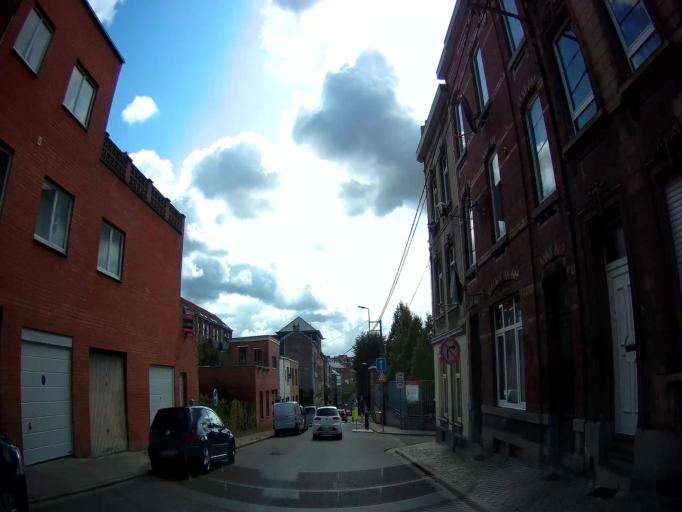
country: BE
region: Wallonia
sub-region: Province de Liege
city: Verviers
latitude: 50.5995
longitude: 5.8608
